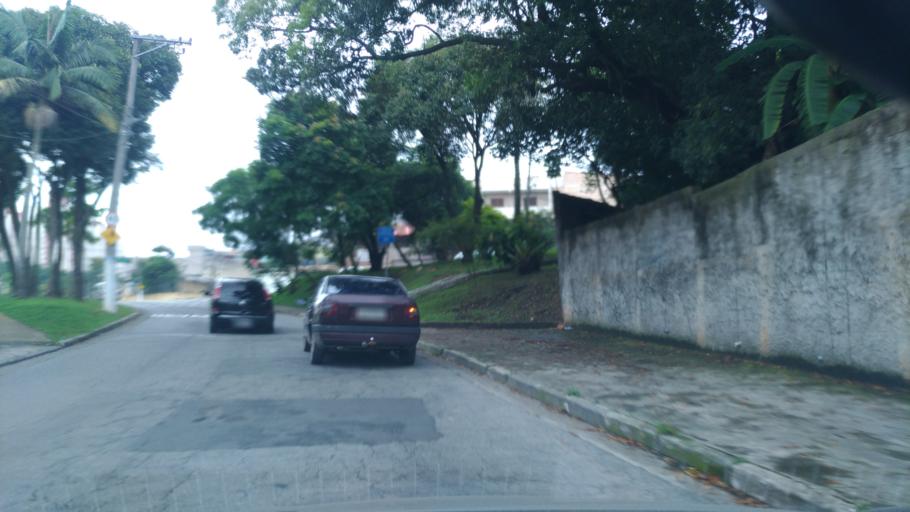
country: BR
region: Sao Paulo
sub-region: Santo Andre
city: Santo Andre
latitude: -23.6925
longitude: -46.5080
